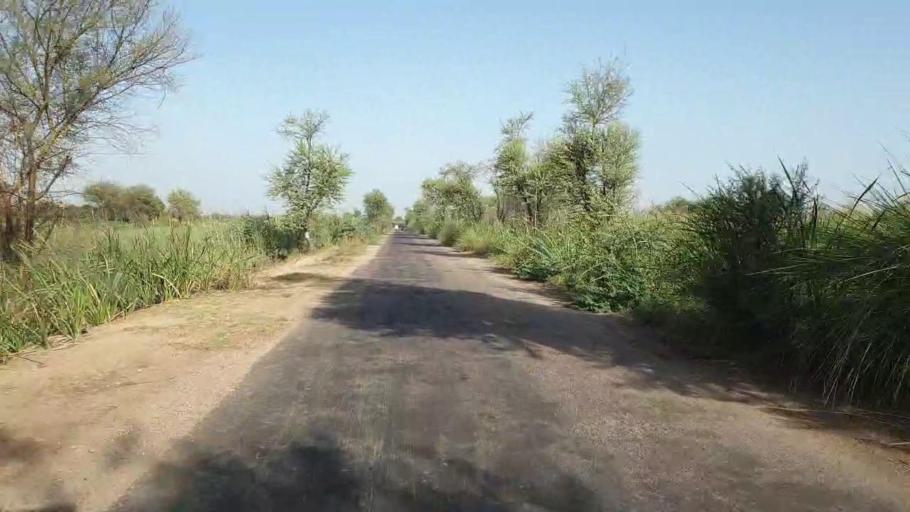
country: PK
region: Sindh
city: Nawabshah
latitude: 26.3778
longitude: 68.4610
